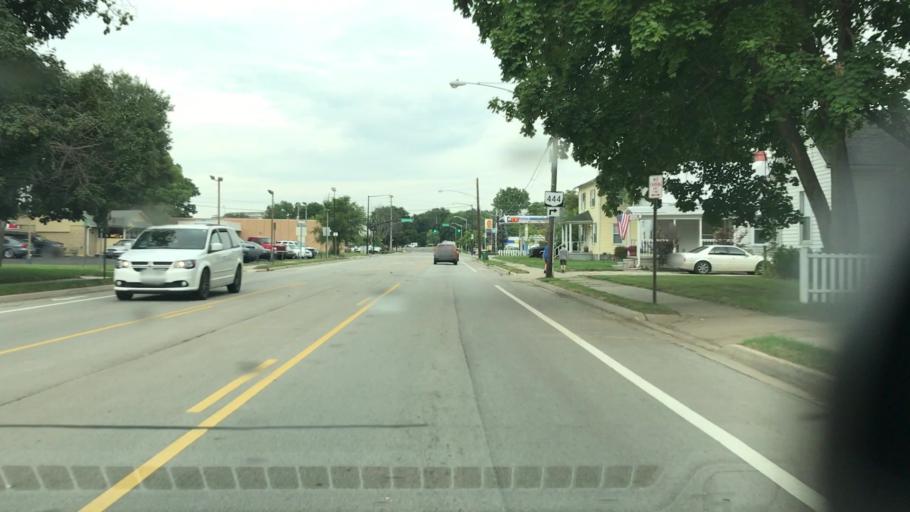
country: US
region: Ohio
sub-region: Greene County
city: Fairborn
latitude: 39.8194
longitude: -84.0231
